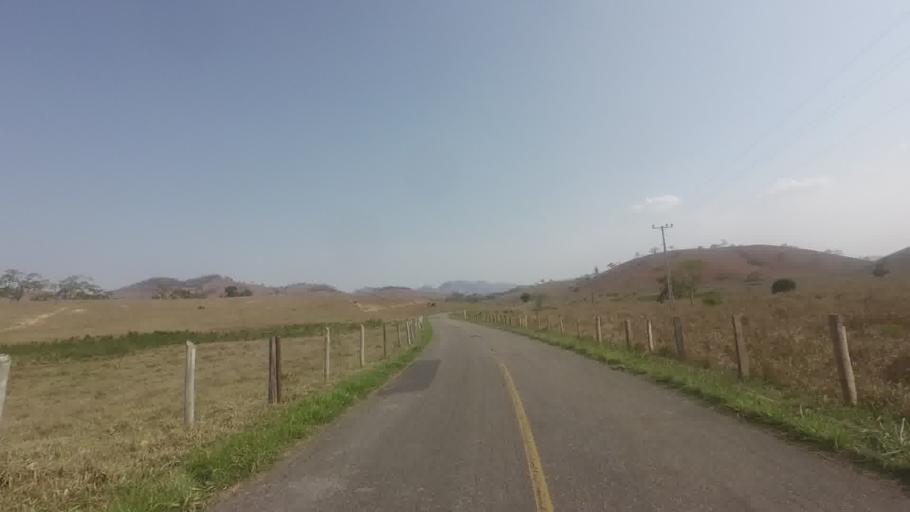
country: BR
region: Rio de Janeiro
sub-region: Bom Jesus Do Itabapoana
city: Bom Jesus do Itabapoana
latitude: -21.1278
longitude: -41.5673
